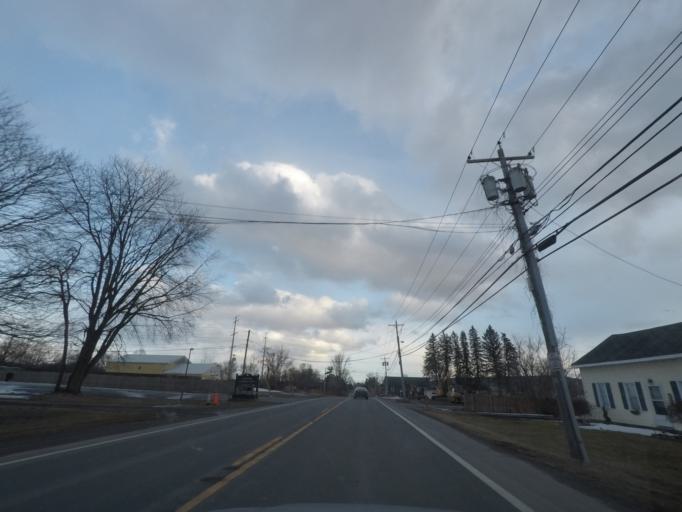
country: US
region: New York
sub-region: Oneida County
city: Utica
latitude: 43.1044
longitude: -75.1628
